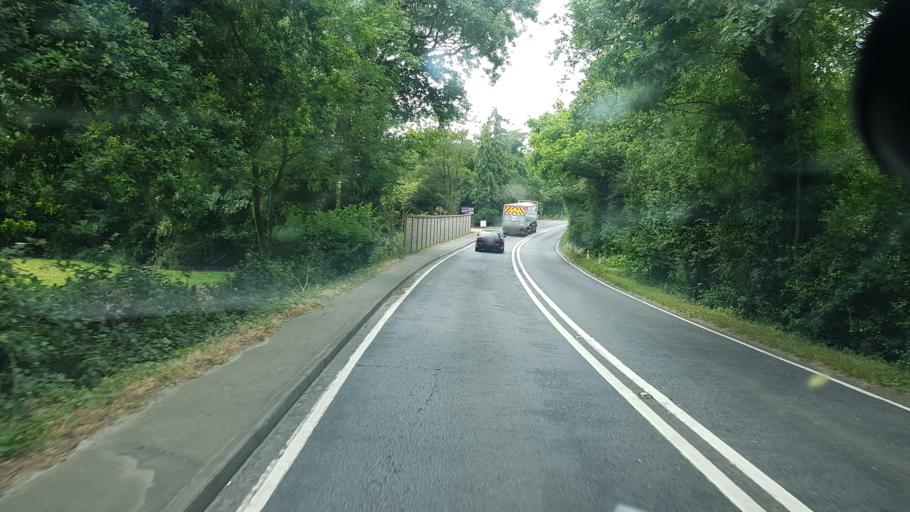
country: GB
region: England
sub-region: Surrey
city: Godstone
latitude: 51.2327
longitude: -0.0482
